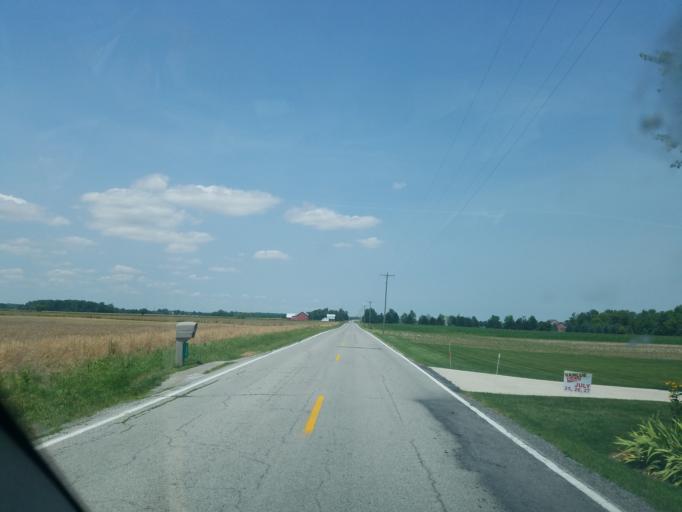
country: US
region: Ohio
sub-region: Wyandot County
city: Carey
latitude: 40.9579
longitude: -83.4861
